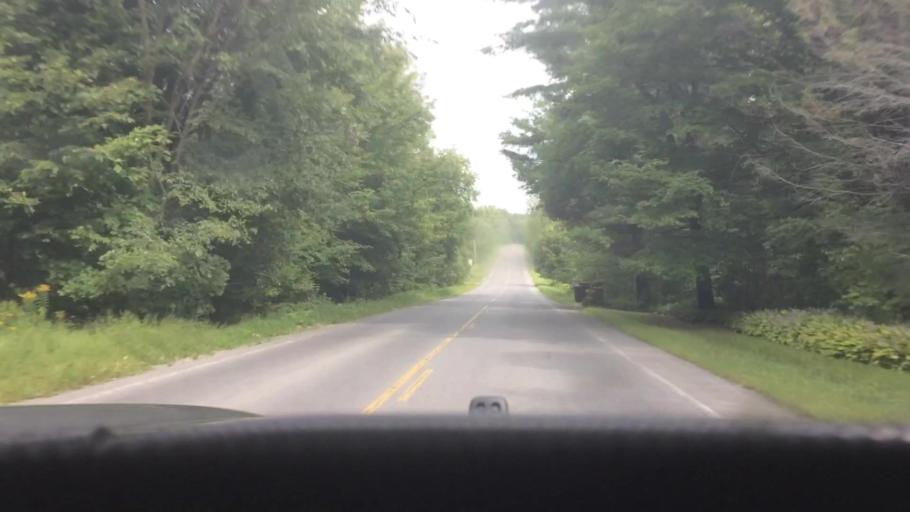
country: US
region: New York
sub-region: St. Lawrence County
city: Canton
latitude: 44.4960
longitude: -75.2163
